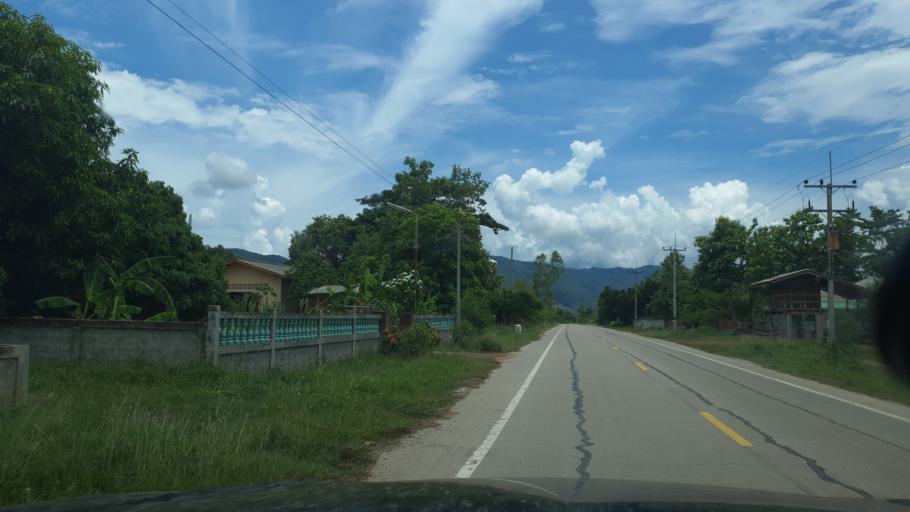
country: TH
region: Lampang
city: Sop Prap
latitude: 17.9202
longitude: 99.4112
